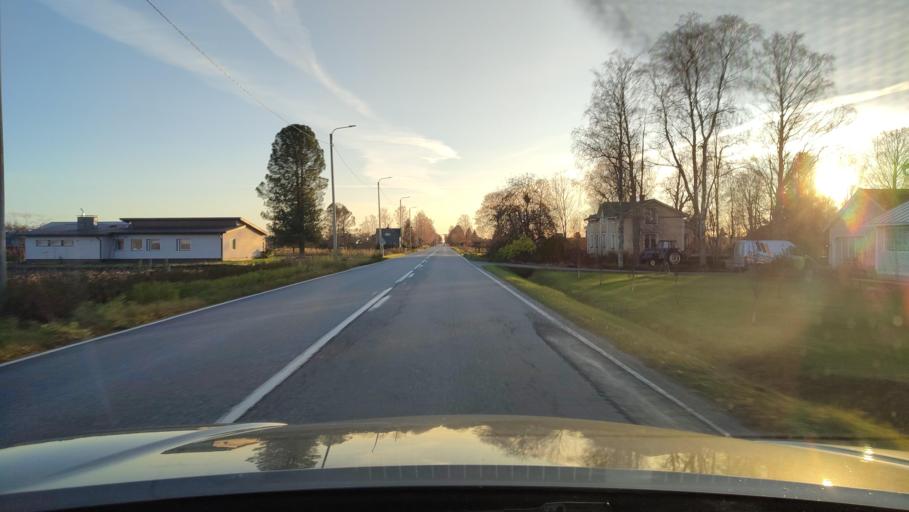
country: FI
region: Ostrobothnia
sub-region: Sydosterbotten
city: Naerpes
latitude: 62.6006
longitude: 21.4548
